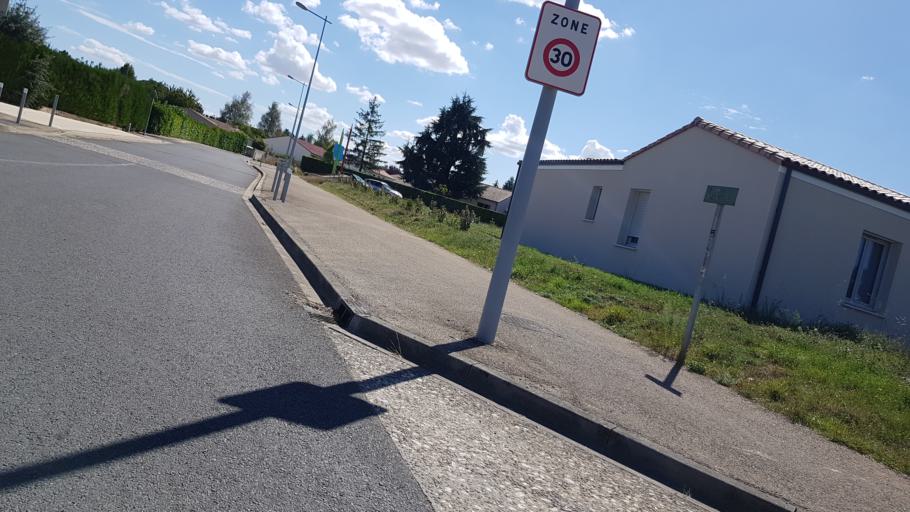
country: FR
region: Poitou-Charentes
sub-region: Departement des Deux-Sevres
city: Vouille
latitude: 46.3149
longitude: -0.3604
